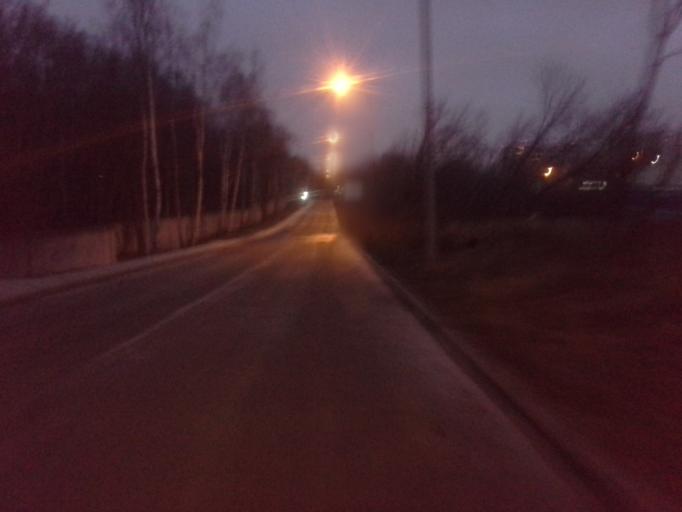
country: RU
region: Moskovskaya
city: Vostryakovo
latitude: 55.6598
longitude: 37.4527
